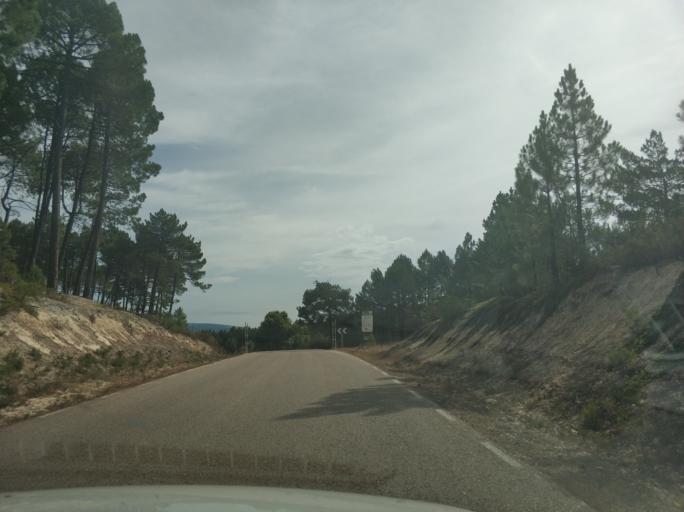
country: ES
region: Castille and Leon
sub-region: Provincia de Soria
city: Navaleno
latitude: 41.8506
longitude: -2.9824
